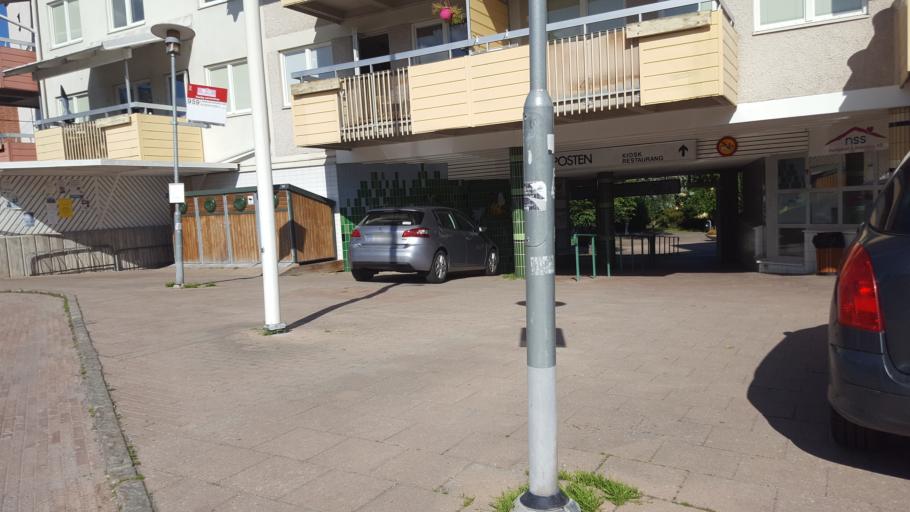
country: SE
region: Stockholm
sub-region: Upplands Vasby Kommun
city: Upplands Vaesby
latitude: 59.5203
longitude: 17.8925
